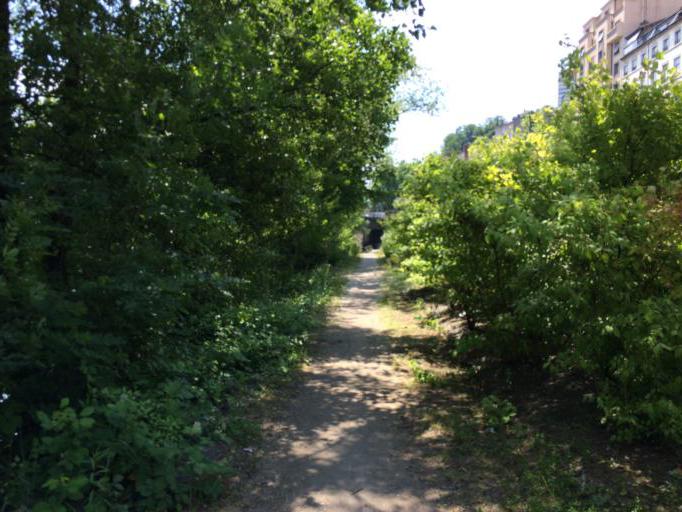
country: FR
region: Rhone-Alpes
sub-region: Departement du Rhone
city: Caluire-et-Cuire
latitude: 45.7805
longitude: 4.8423
